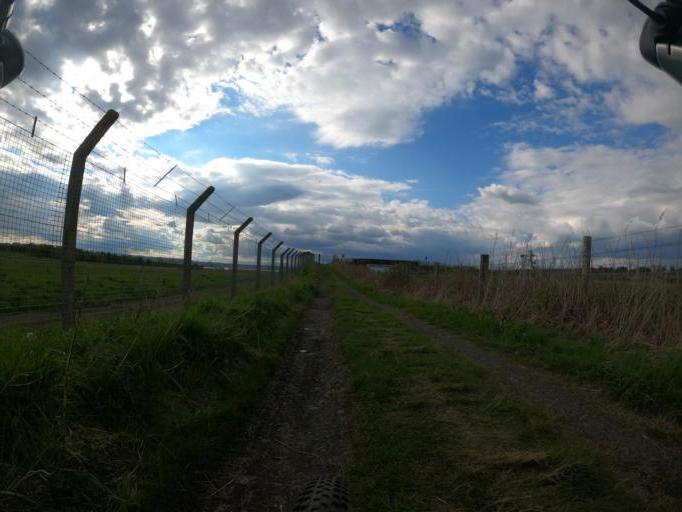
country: GB
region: Scotland
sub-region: Edinburgh
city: Currie
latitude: 55.9434
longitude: -3.3283
